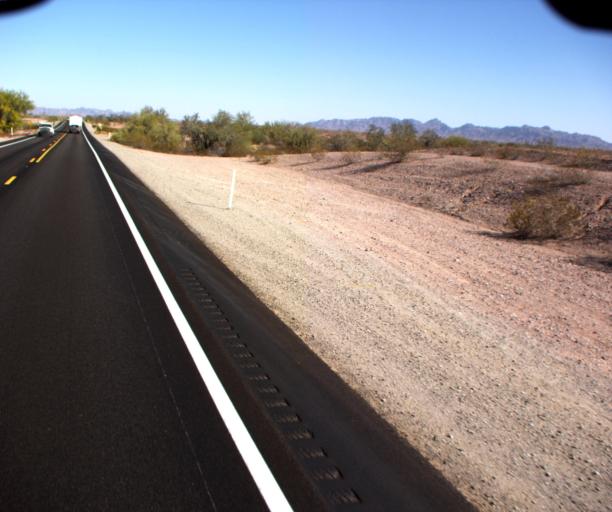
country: US
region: Arizona
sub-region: Yuma County
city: Wellton
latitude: 33.0359
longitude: -114.2891
